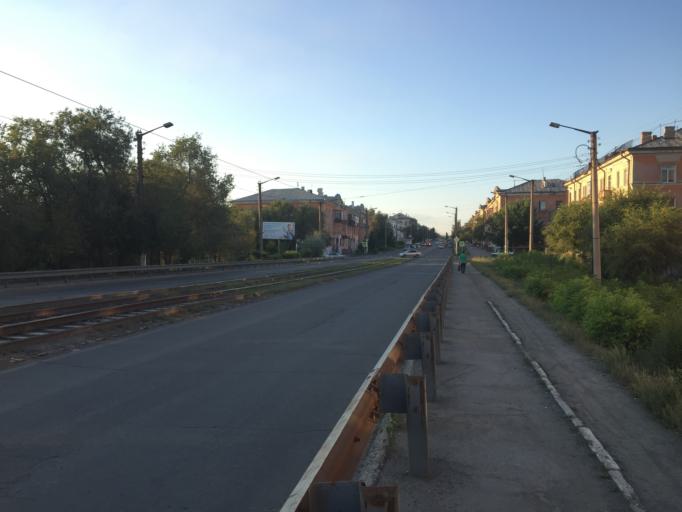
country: RU
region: Orenburg
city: Novotroitsk
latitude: 51.2025
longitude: 58.2991
